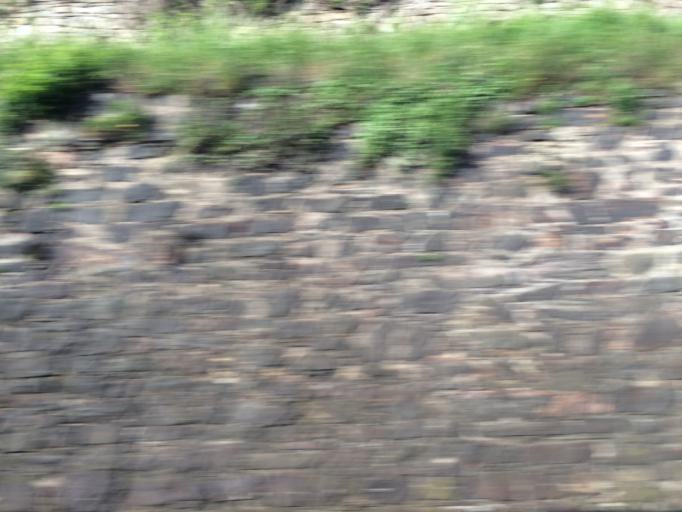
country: DE
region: Rheinland-Pfalz
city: Trechtingshausen
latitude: 50.0152
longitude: 7.8526
